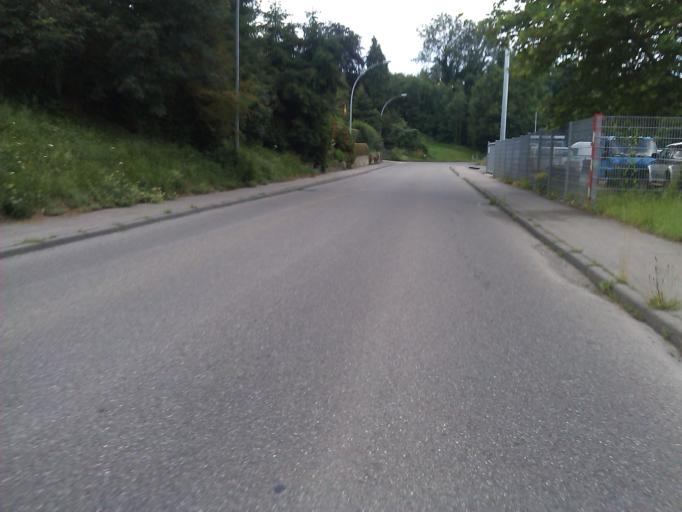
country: DE
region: Baden-Wuerttemberg
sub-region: Regierungsbezirk Stuttgart
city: Bonnigheim
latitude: 49.0732
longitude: 9.1050
